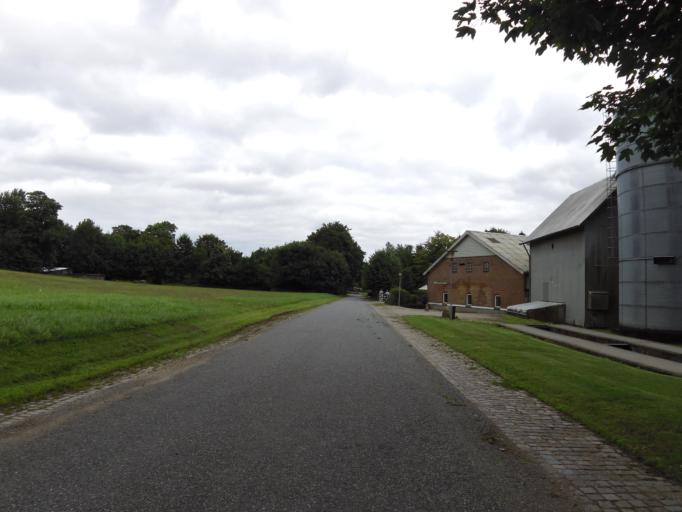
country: DK
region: South Denmark
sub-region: Haderslev Kommune
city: Gram
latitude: 55.2989
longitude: 9.1703
